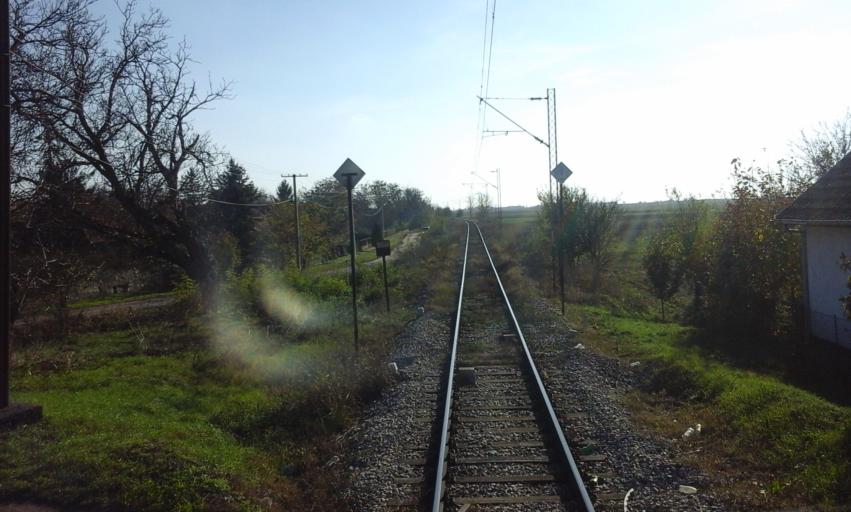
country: RS
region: Autonomna Pokrajina Vojvodina
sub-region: Severnobacki Okrug
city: Backa Topola
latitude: 45.8048
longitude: 19.6476
